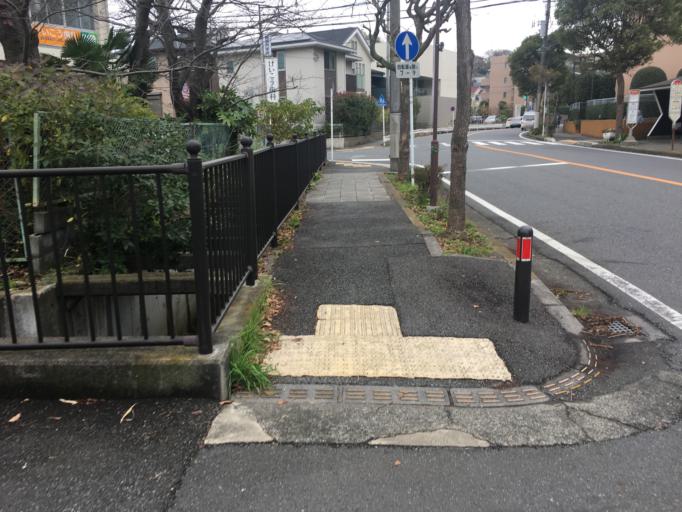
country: JP
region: Kanagawa
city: Kamakura
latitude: 35.3277
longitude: 139.5254
